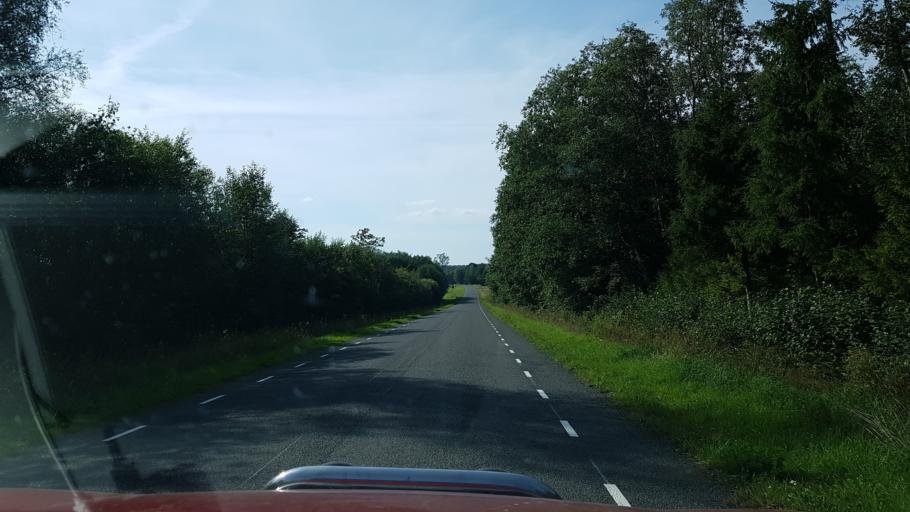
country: EE
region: Viljandimaa
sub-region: Abja vald
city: Abja-Paluoja
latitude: 58.3380
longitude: 25.2506
